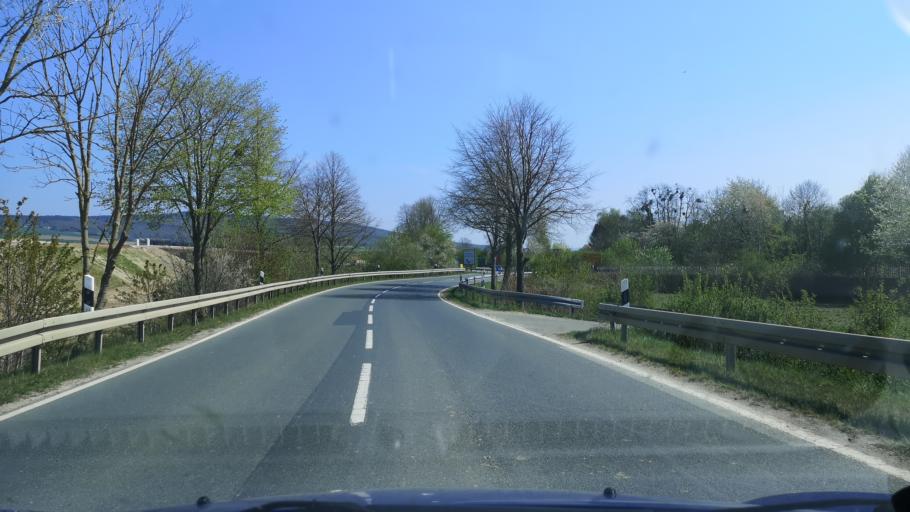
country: DE
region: Lower Saxony
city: Coppenbrugge
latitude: 52.1221
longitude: 9.5301
